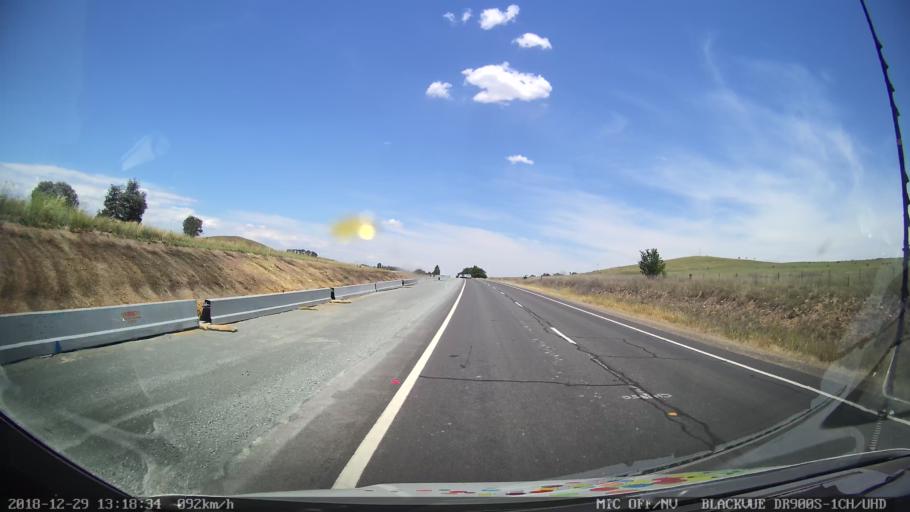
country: AU
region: Australian Capital Territory
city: Macarthur
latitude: -35.7531
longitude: 149.1609
